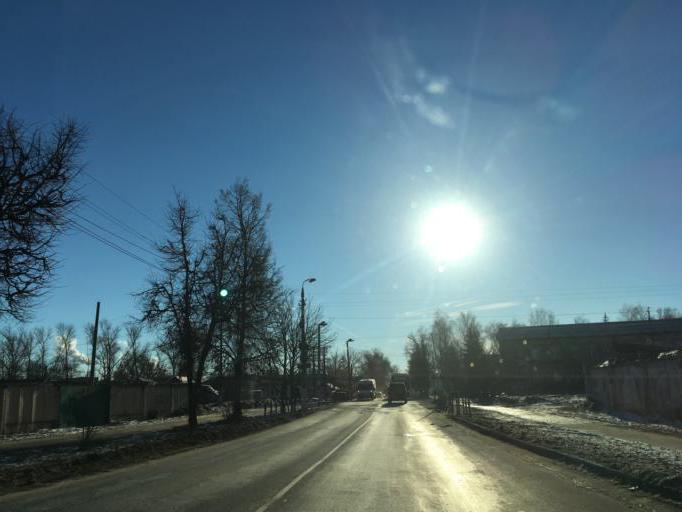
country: RU
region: Tula
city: Tula
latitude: 54.1779
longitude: 37.7051
